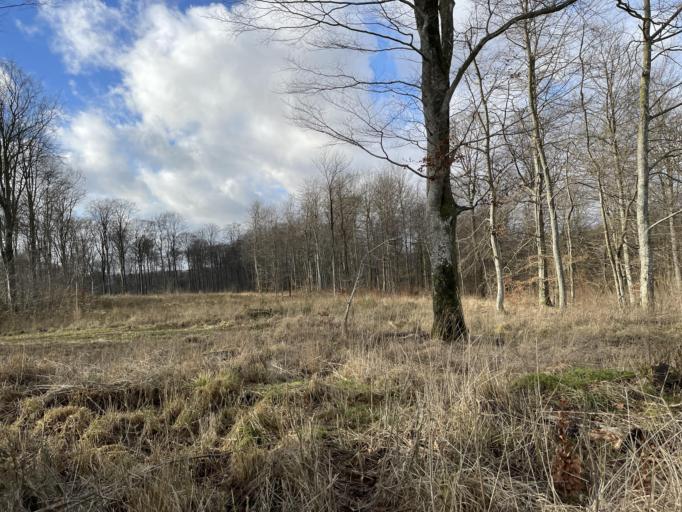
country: DK
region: Central Jutland
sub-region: Viborg Kommune
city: Bjerringbro
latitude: 56.2574
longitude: 9.6813
